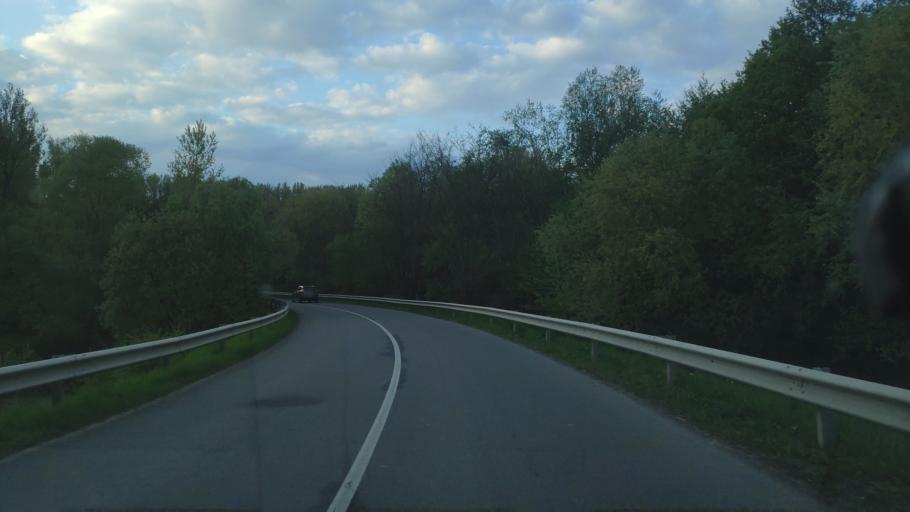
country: SK
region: Presovsky
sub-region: Okres Presov
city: Presov
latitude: 48.8997
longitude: 21.2627
